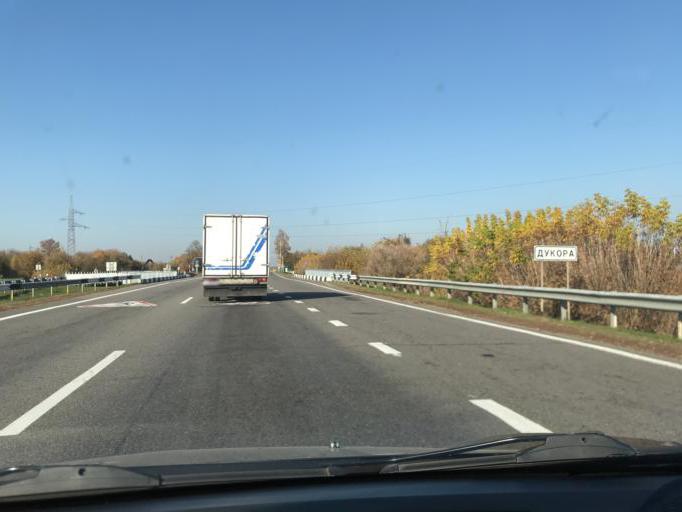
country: BY
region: Minsk
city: Dukora
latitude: 53.6667
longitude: 27.9380
